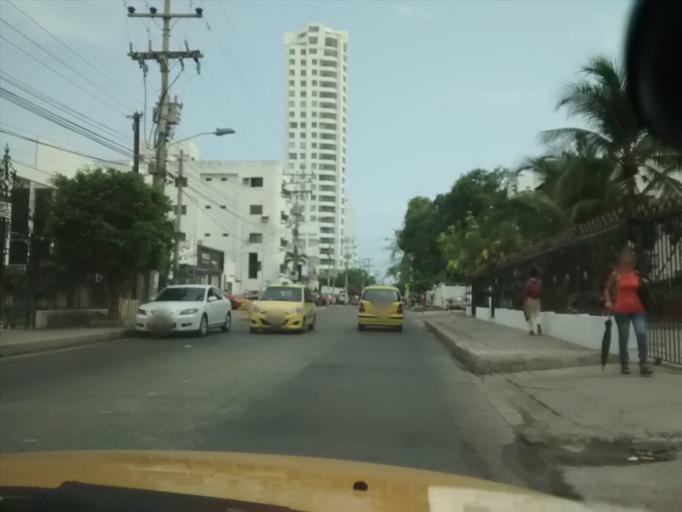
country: CO
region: Bolivar
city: Cartagena
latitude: 10.4122
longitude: -75.5367
